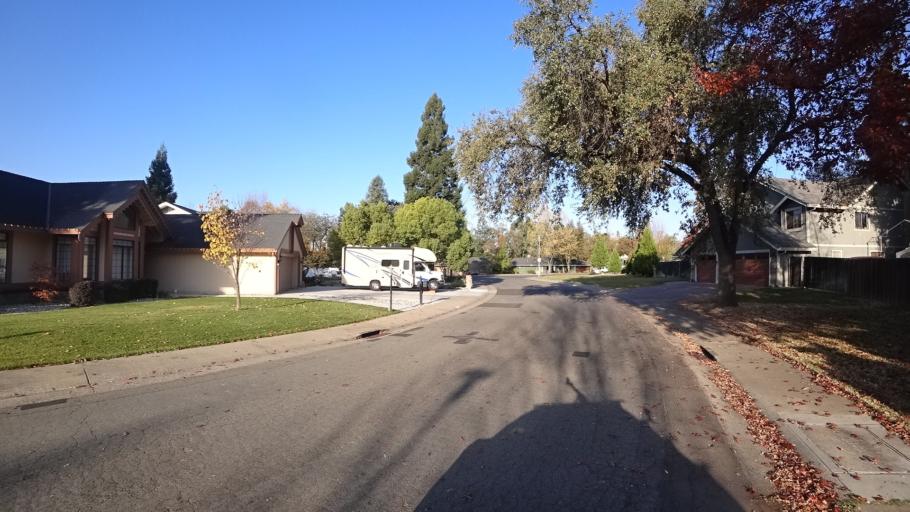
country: US
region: California
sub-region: Sacramento County
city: Citrus Heights
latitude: 38.6969
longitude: -121.2602
